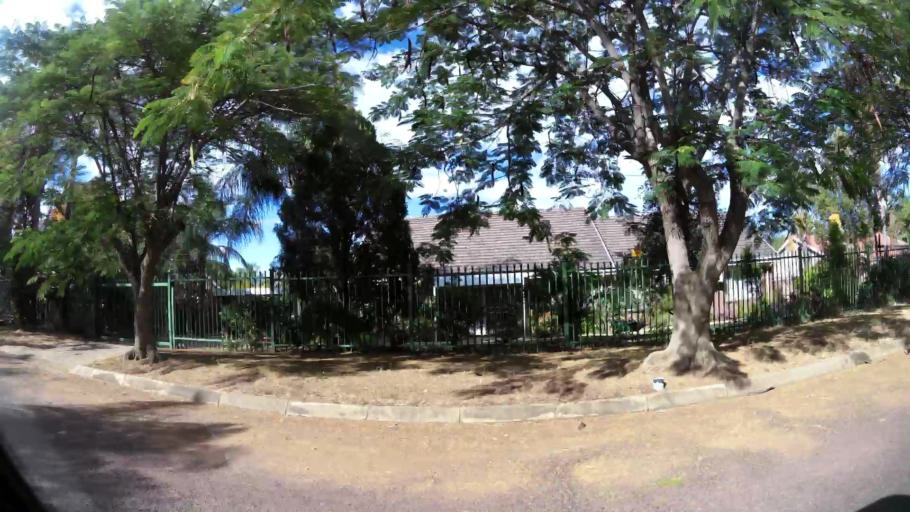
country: ZA
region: Limpopo
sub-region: Waterberg District Municipality
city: Warmbaths
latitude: -24.8756
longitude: 28.2842
